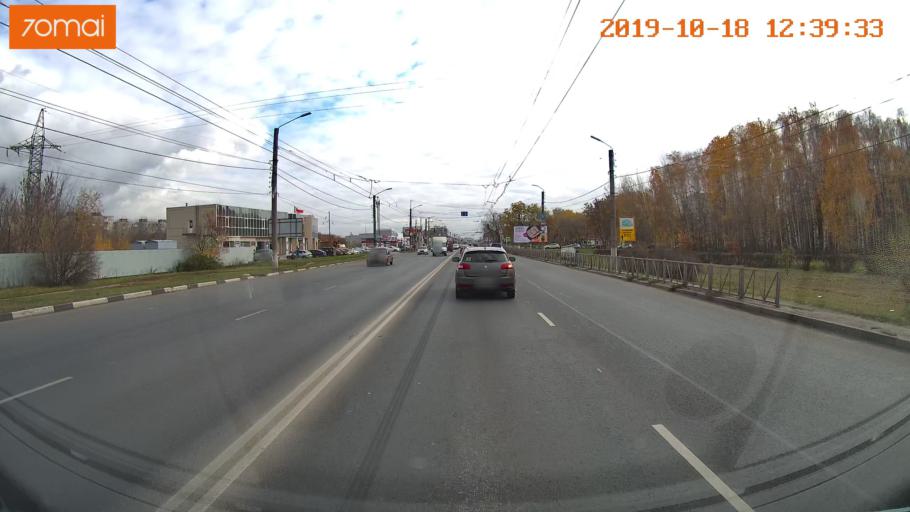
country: RU
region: Rjazan
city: Ryazan'
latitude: 54.6498
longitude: 39.6459
